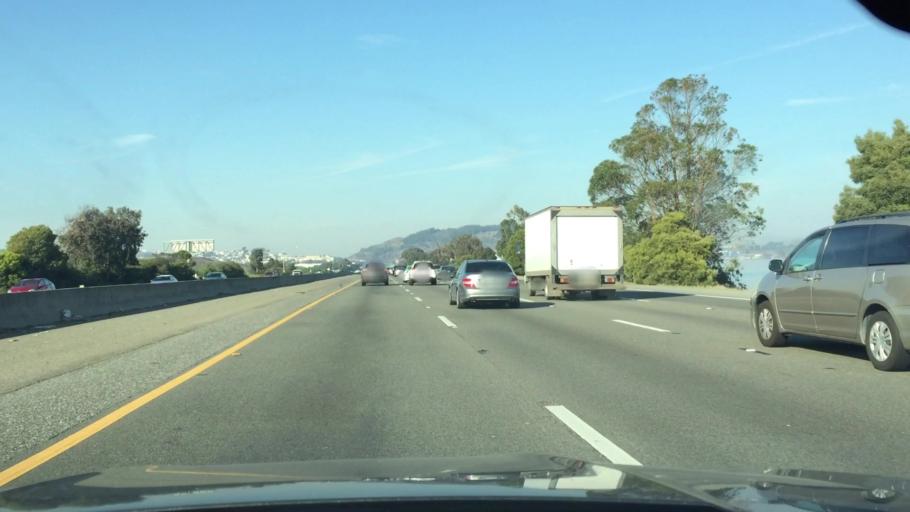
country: US
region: California
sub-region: San Mateo County
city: Brisbane
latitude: 37.6852
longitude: -122.3891
